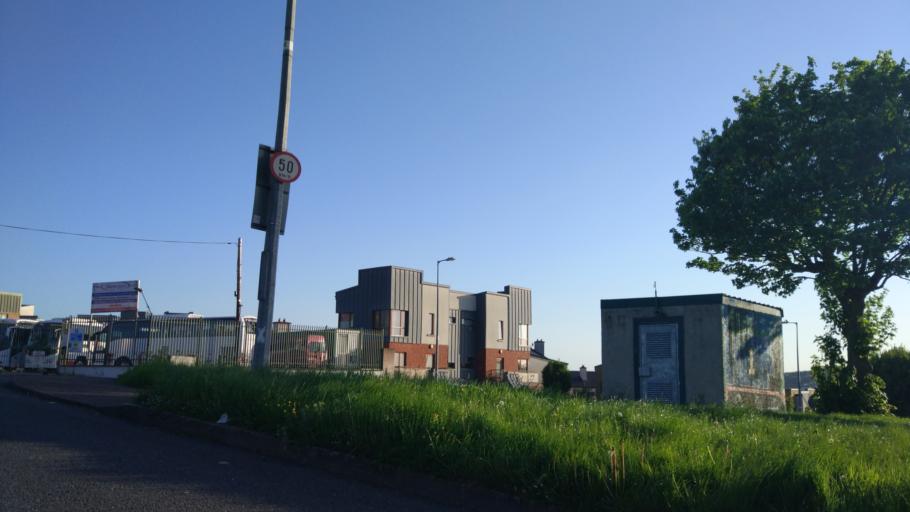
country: IE
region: Munster
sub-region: County Cork
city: Cork
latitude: 51.9111
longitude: -8.4657
